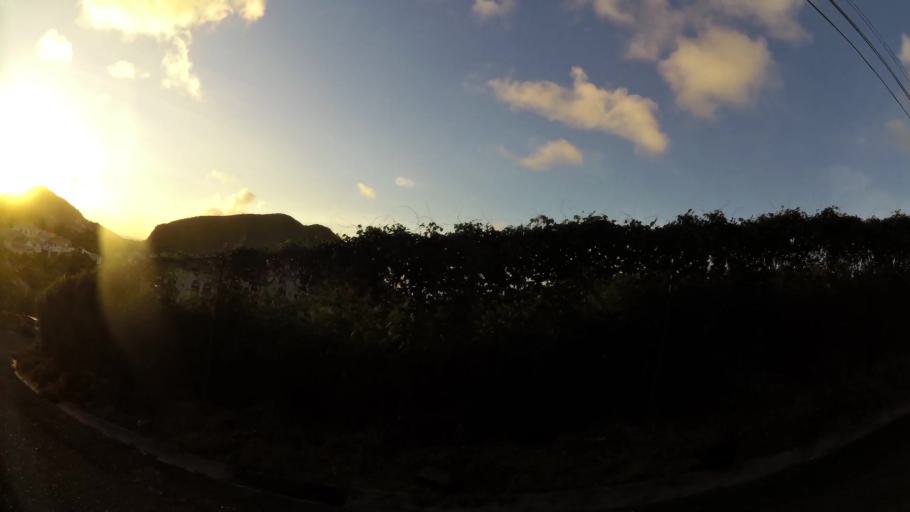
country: LC
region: Gros-Islet
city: Gros Islet
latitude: 14.0653
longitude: -60.9504
